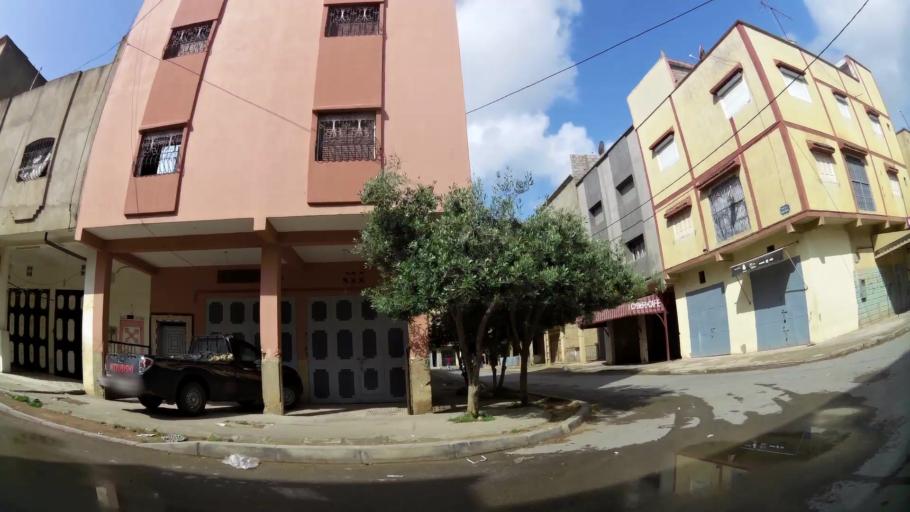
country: MA
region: Rabat-Sale-Zemmour-Zaer
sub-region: Khemisset
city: Tiflet
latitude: 33.8973
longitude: -6.3188
